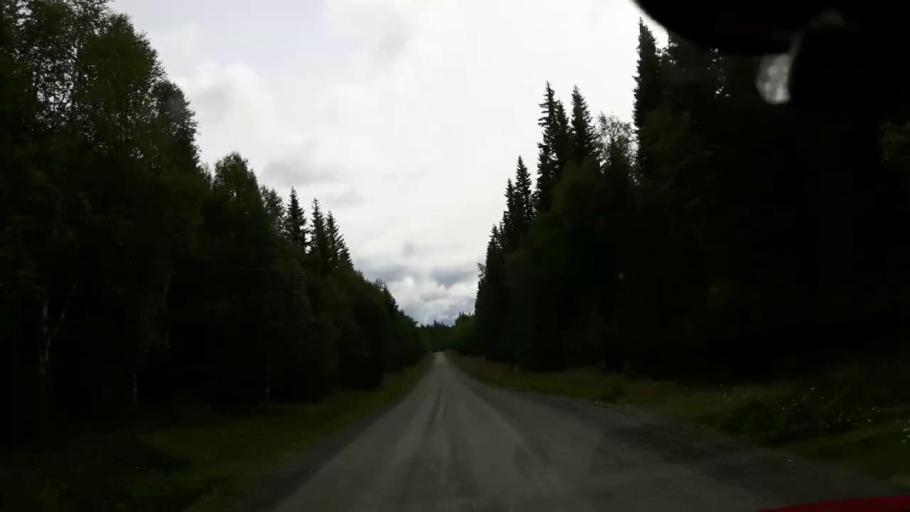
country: SE
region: Jaemtland
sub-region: Krokoms Kommun
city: Valla
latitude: 63.6604
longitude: 13.9707
